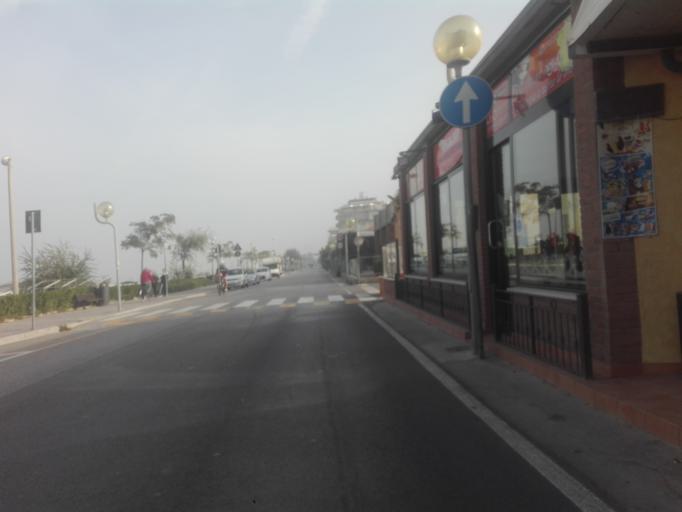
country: IT
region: Emilia-Romagna
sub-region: Provincia di Rimini
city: Rimini
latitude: 44.0820
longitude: 12.5474
